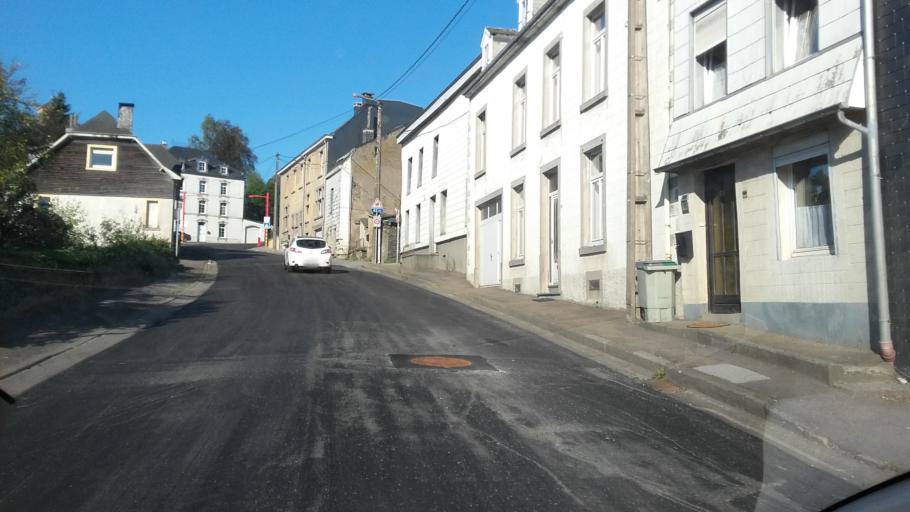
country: BE
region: Wallonia
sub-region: Province du Luxembourg
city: Neufchateau
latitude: 49.8398
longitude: 5.4375
